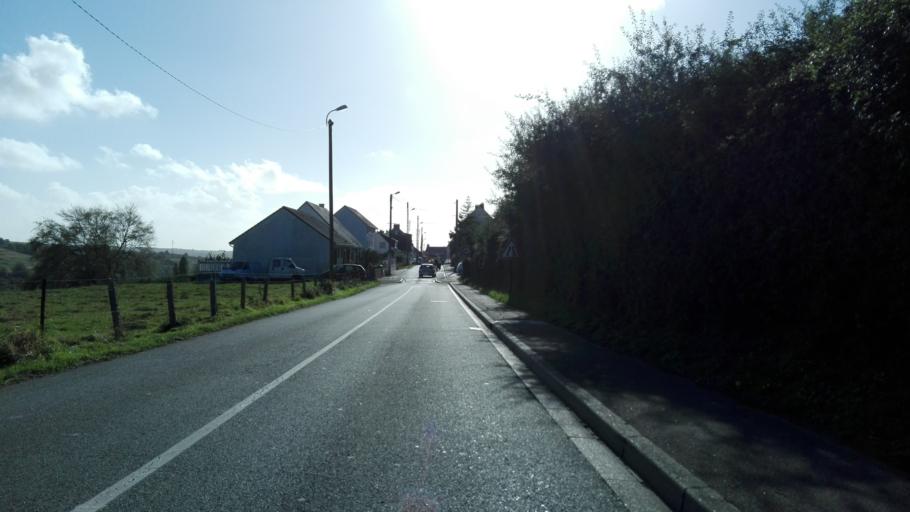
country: FR
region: Nord-Pas-de-Calais
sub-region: Departement du Pas-de-Calais
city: Boulogne-sur-Mer
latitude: 50.7114
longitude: 1.6271
